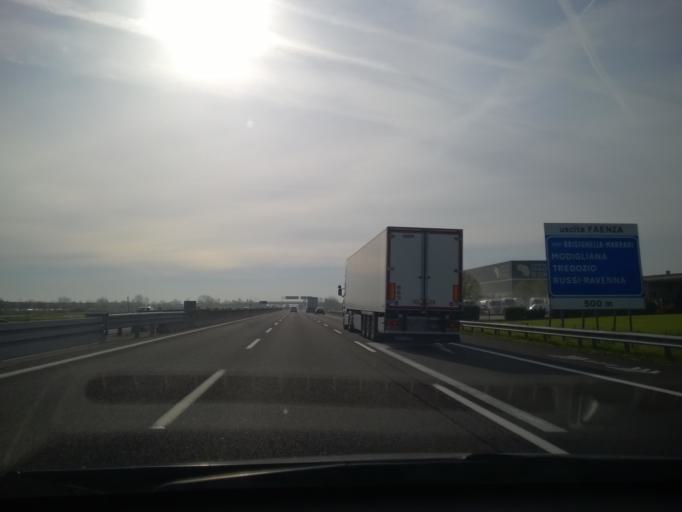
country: IT
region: Emilia-Romagna
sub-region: Provincia di Ravenna
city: Faenza
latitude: 44.3265
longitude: 11.8981
